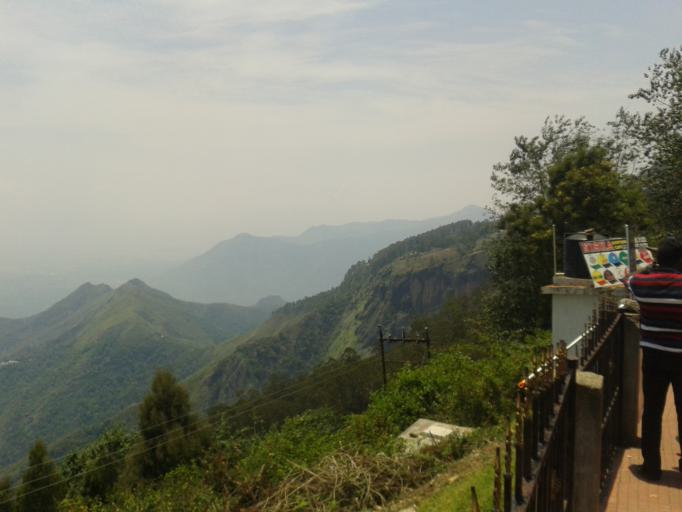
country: IN
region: Tamil Nadu
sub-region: Dindigul
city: Kodaikanal
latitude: 10.2282
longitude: 77.4930
